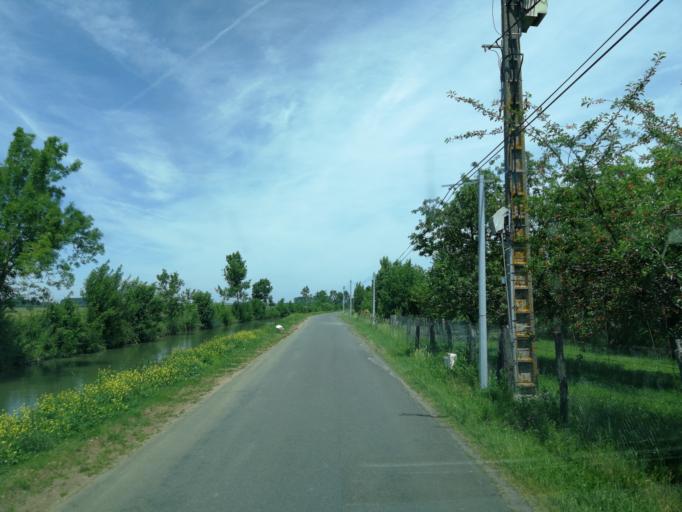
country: FR
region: Pays de la Loire
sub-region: Departement de la Vendee
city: Le Langon
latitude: 46.4066
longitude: -0.9250
